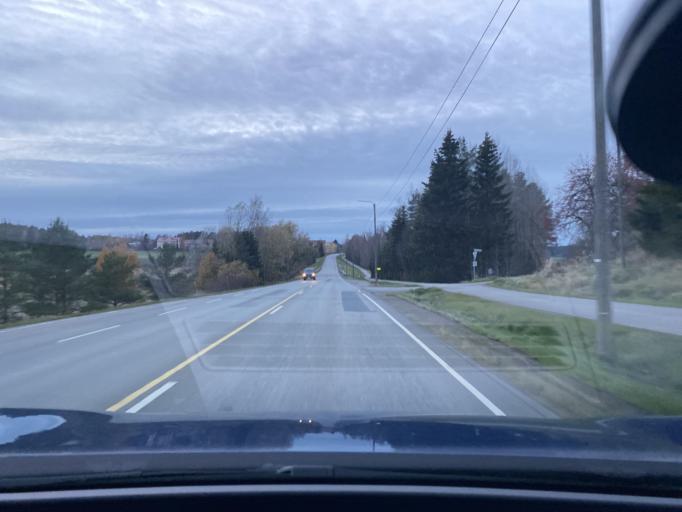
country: FI
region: Uusimaa
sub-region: Helsinki
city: Saukkola
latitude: 60.3850
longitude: 23.9255
